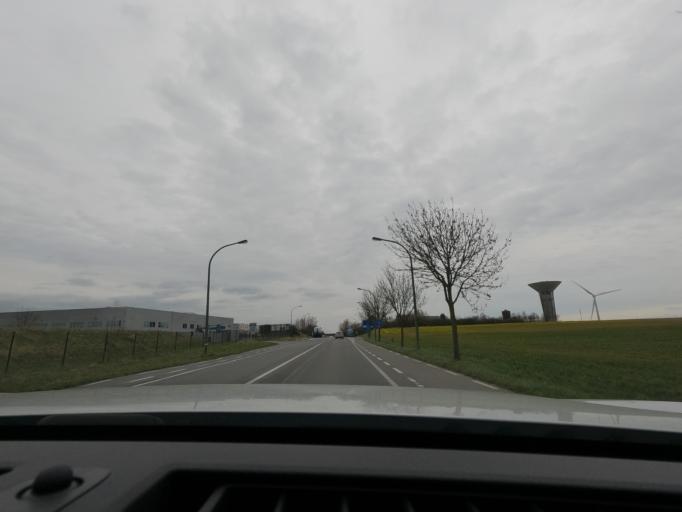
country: BE
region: Wallonia
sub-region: Province du Hainaut
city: Silly
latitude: 50.6674
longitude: 3.8718
